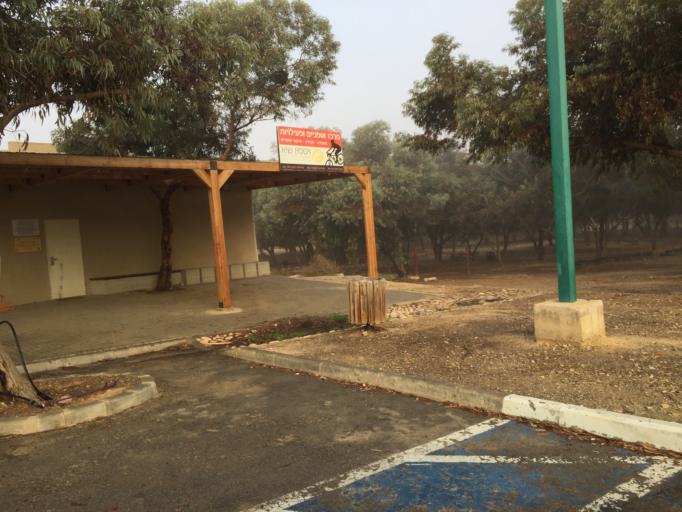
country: IL
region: Southern District
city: Yeroham
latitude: 30.9905
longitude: 34.9103
